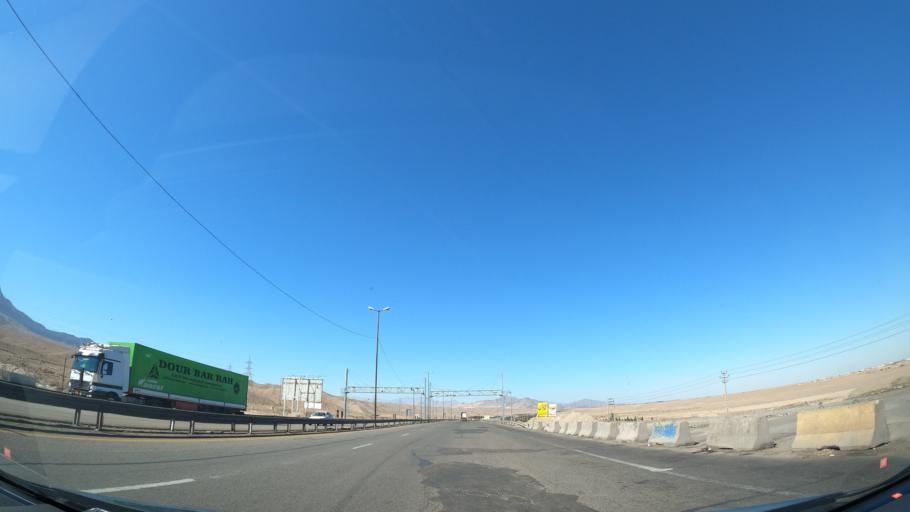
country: IR
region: Isfahan
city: Kashan
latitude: 33.9591
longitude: 51.3542
